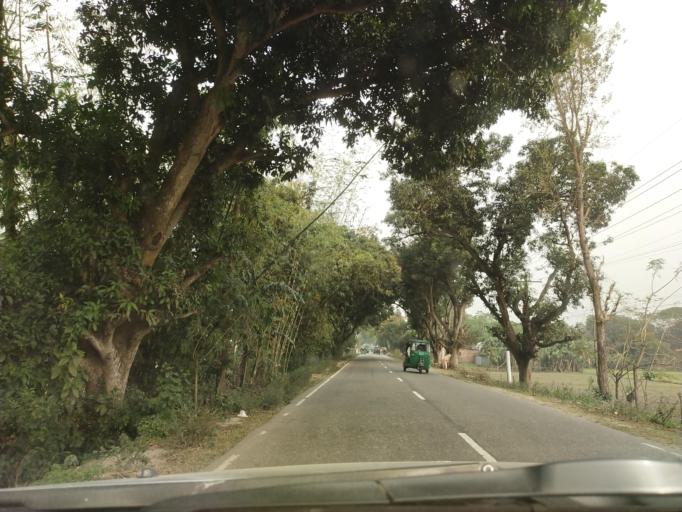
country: BD
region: Dhaka
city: Narsingdi
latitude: 24.0060
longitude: 90.7374
